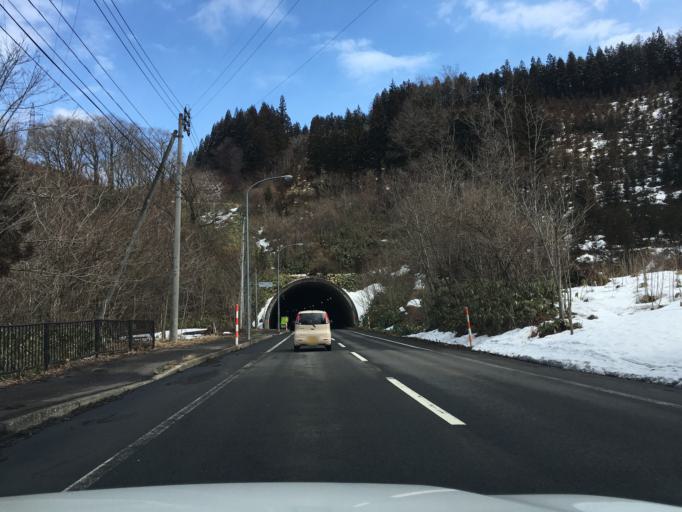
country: JP
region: Akita
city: Takanosu
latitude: 40.0003
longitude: 140.2740
